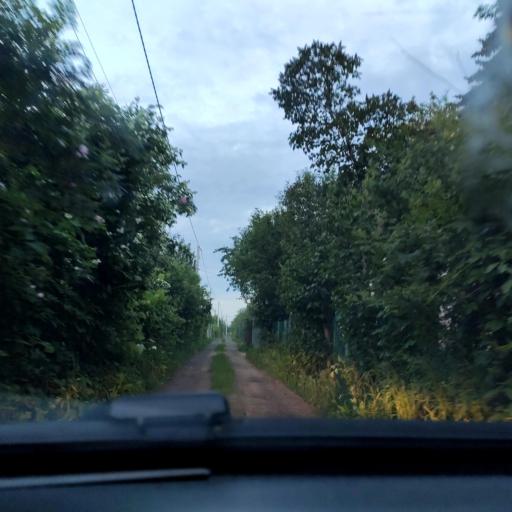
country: RU
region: Voronezj
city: Shilovo
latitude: 51.5873
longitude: 39.1603
